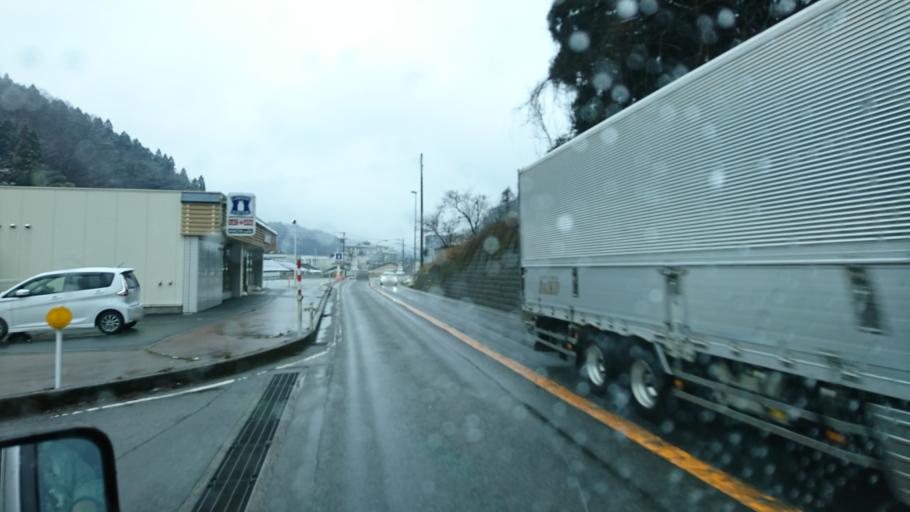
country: JP
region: Tottori
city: Tottori
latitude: 35.5511
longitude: 134.4942
